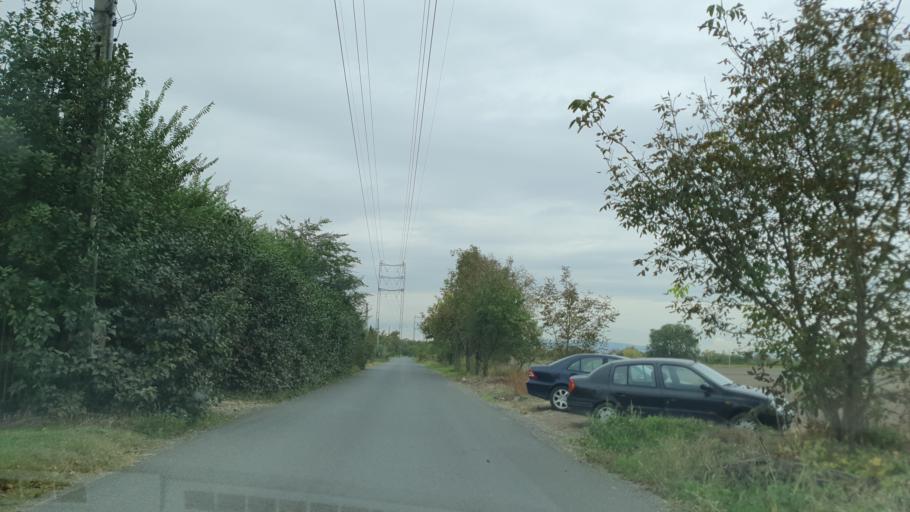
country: HU
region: Pest
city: Dunaharaszti
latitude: 47.3801
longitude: 19.0829
